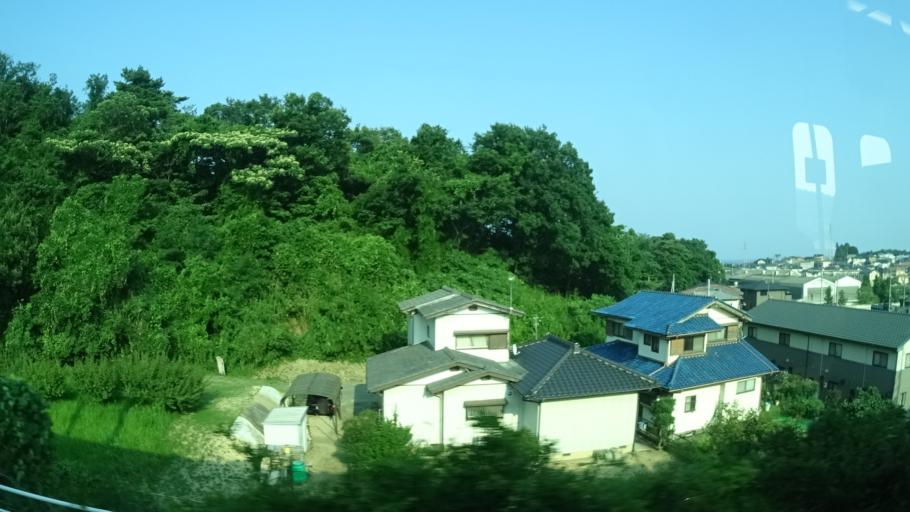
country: JP
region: Ibaraki
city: Hitachi
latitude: 36.6119
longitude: 140.6699
